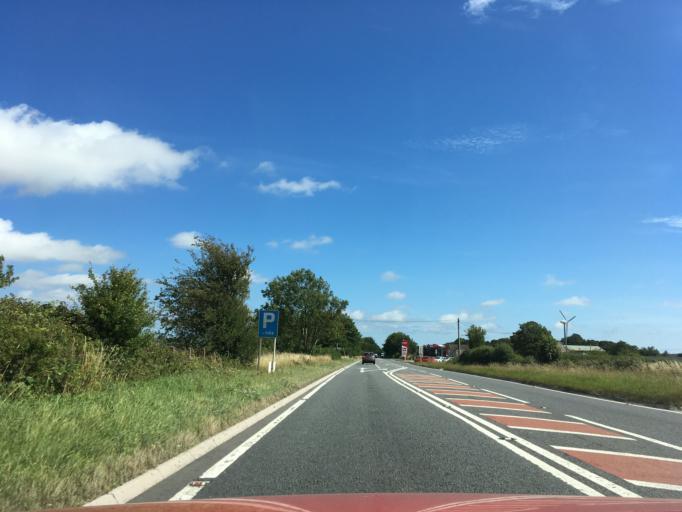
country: GB
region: England
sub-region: Dorset
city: Dorchester
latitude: 50.7604
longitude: -2.5264
